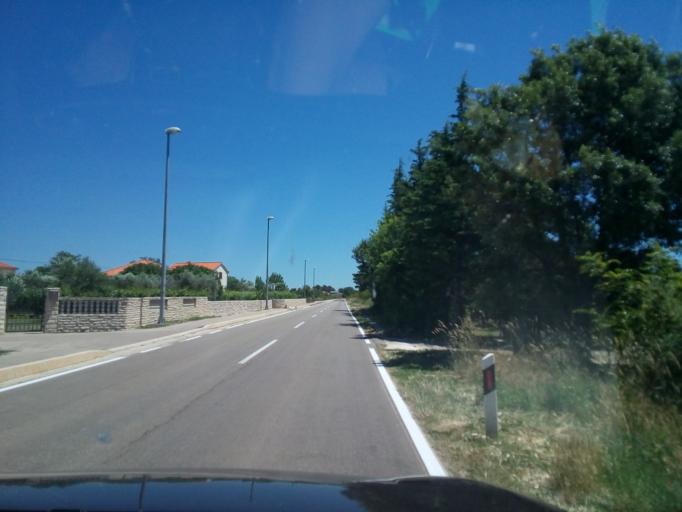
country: HR
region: Zadarska
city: Nin
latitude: 44.2260
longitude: 15.2019
